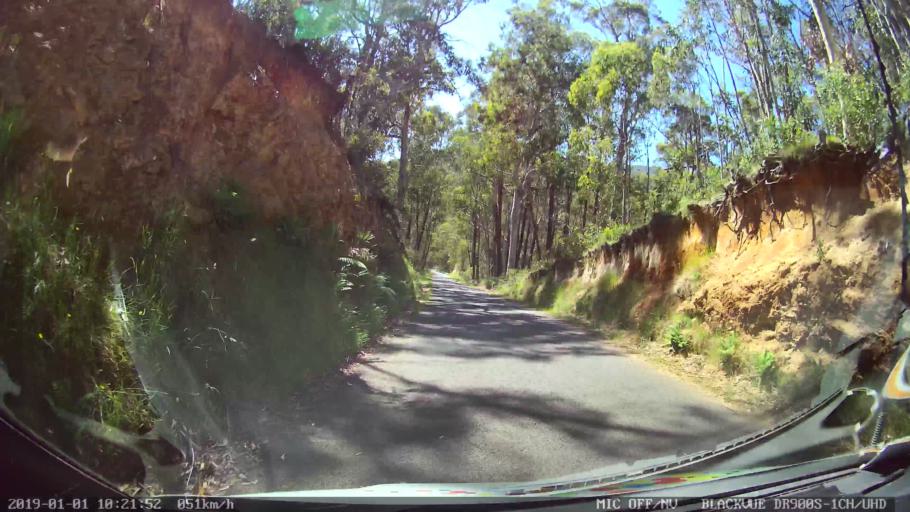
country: AU
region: New South Wales
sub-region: Snowy River
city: Jindabyne
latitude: -36.0782
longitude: 148.1981
